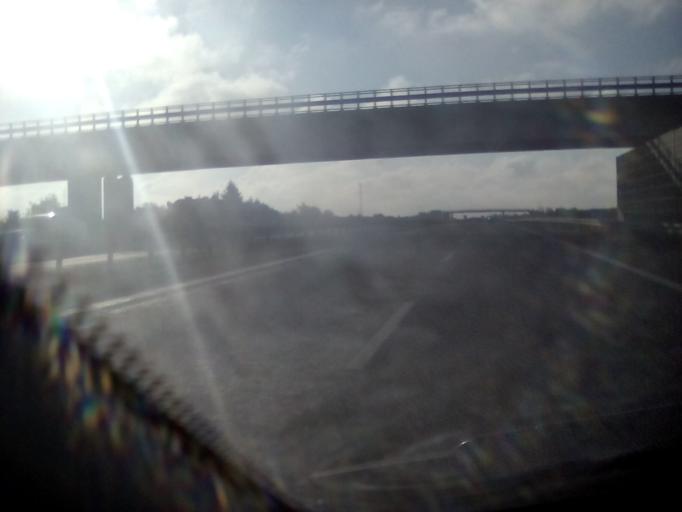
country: PL
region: Masovian Voivodeship
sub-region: Powiat grojecki
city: Jasieniec
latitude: 51.7870
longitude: 20.8937
